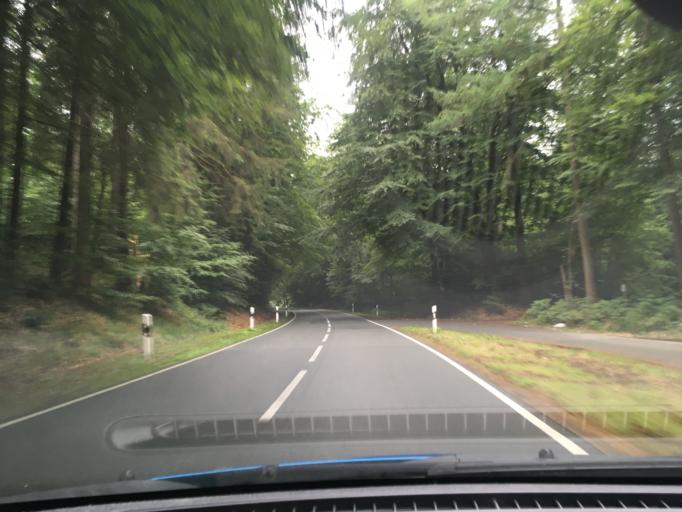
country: DE
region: Lower Saxony
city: Garlstorf
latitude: 53.2222
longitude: 10.0827
